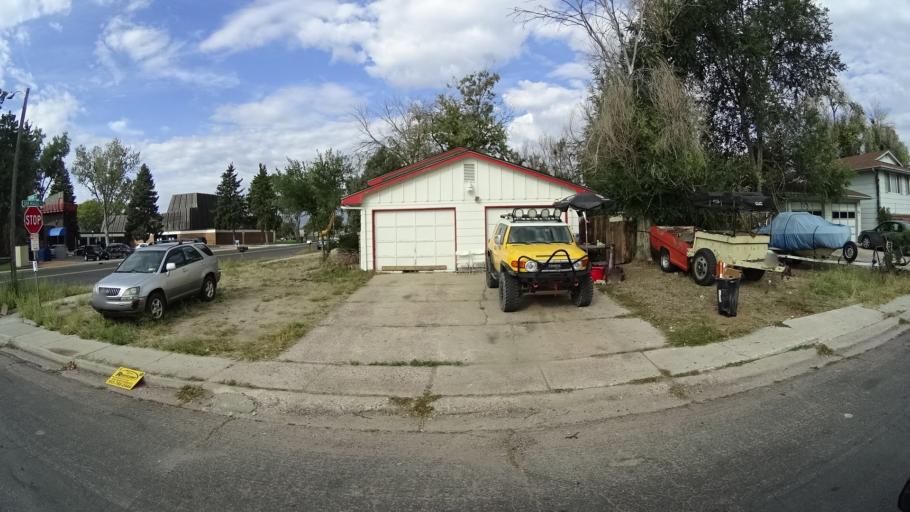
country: US
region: Colorado
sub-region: El Paso County
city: Cimarron Hills
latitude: 38.8510
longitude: -104.7499
